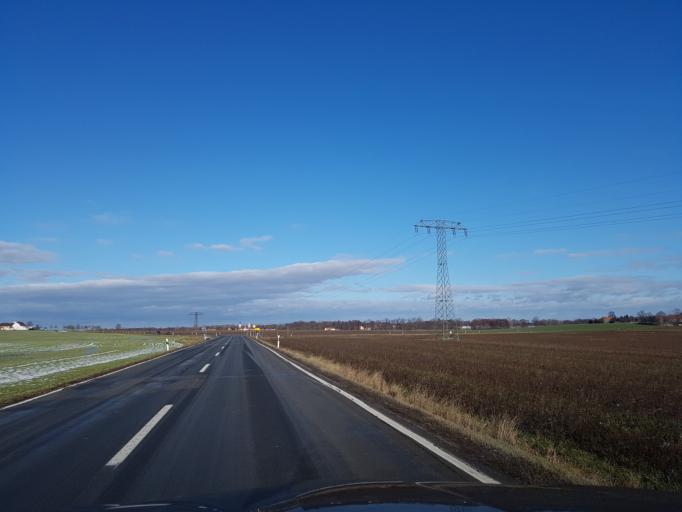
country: DE
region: Saxony
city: Priestewitz
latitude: 51.2346
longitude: 13.5559
